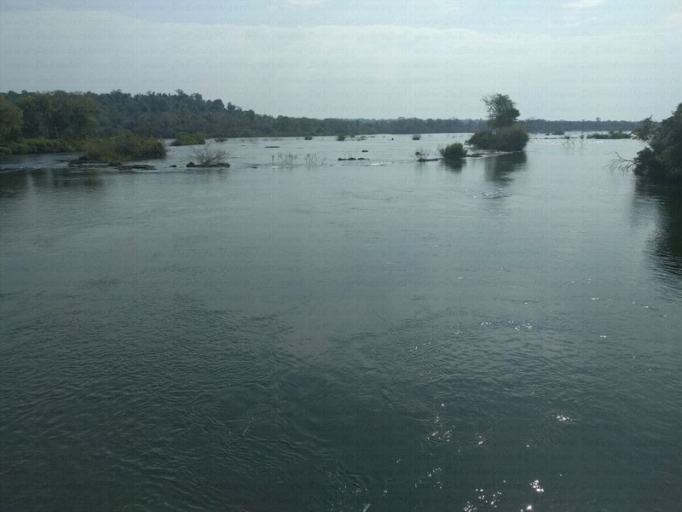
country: AR
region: Misiones
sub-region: Departamento de Iguazu
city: Puerto Iguazu
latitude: -25.6984
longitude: -54.4412
